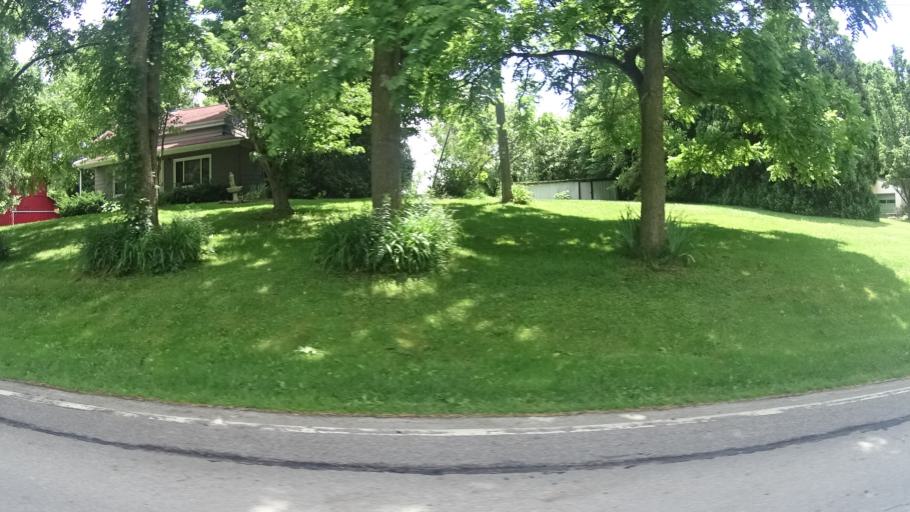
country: US
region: Ohio
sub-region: Erie County
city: Milan
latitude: 41.2996
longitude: -82.5974
